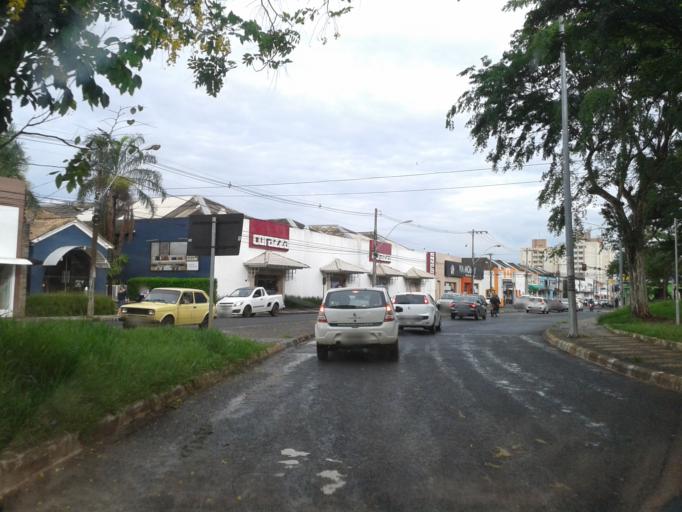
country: BR
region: Minas Gerais
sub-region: Uberlandia
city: Uberlandia
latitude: -18.9109
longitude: -48.2770
